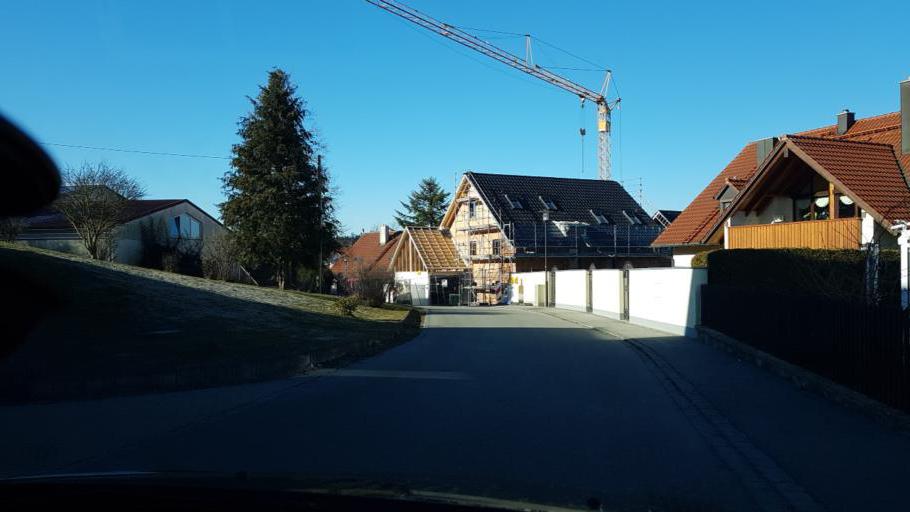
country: DE
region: Bavaria
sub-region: Upper Bavaria
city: Oberschweinbach
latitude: 48.2388
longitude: 11.1580
